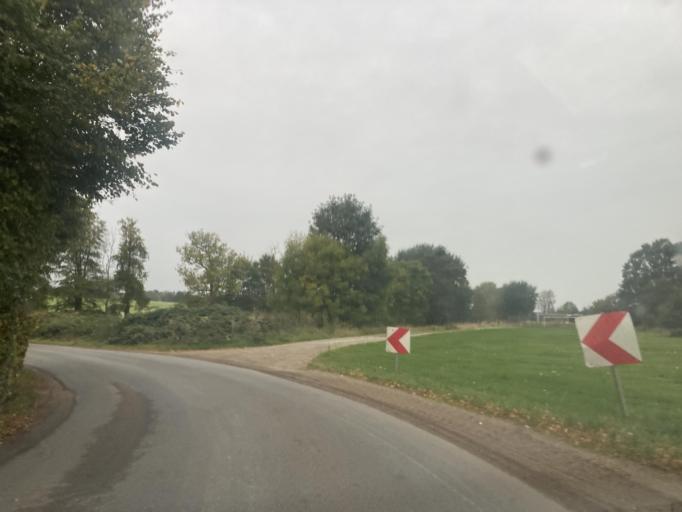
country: DK
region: Capital Region
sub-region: Egedal Kommune
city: Vekso
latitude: 55.7277
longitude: 12.2158
